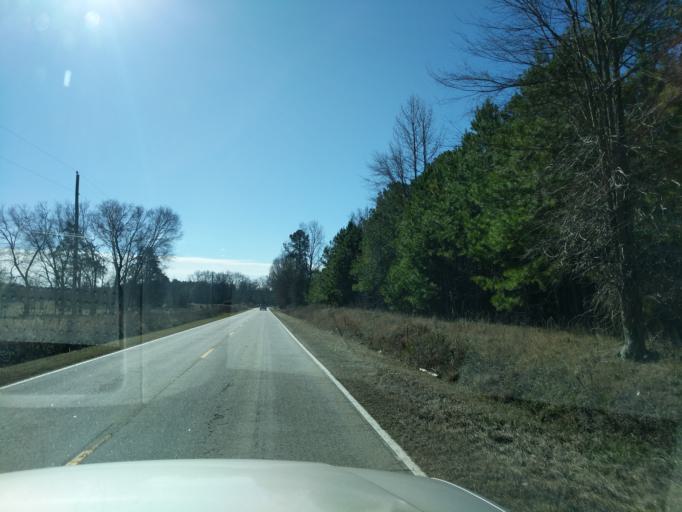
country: US
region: South Carolina
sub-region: Laurens County
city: Joanna
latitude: 34.2941
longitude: -81.8445
